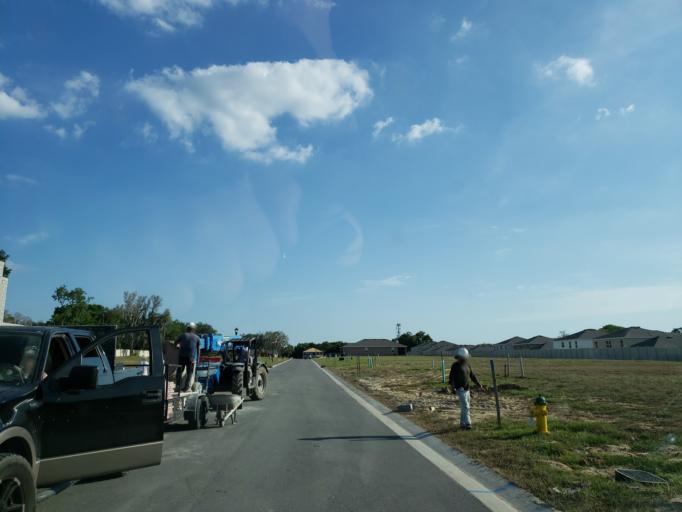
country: US
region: Florida
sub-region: Hillsborough County
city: Brandon
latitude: 27.9114
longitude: -82.2821
